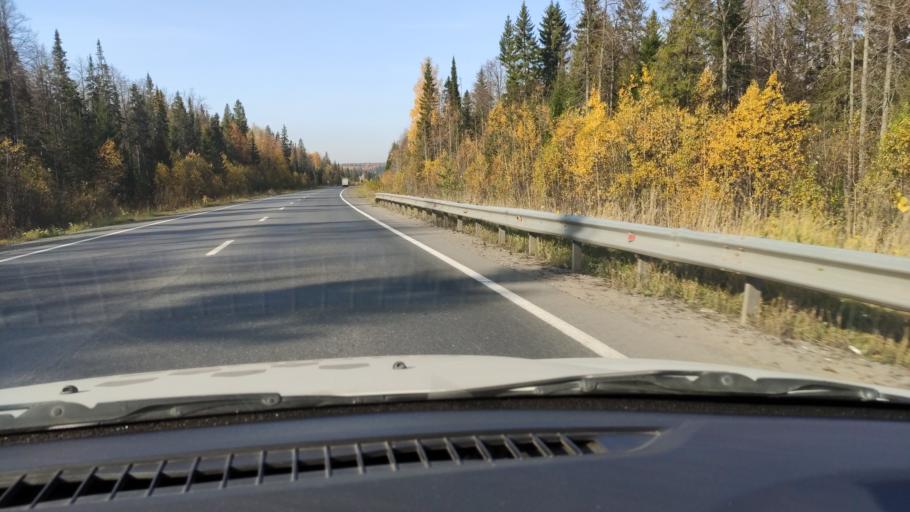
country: RU
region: Perm
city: Novyye Lyady
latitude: 58.0334
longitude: 56.4788
